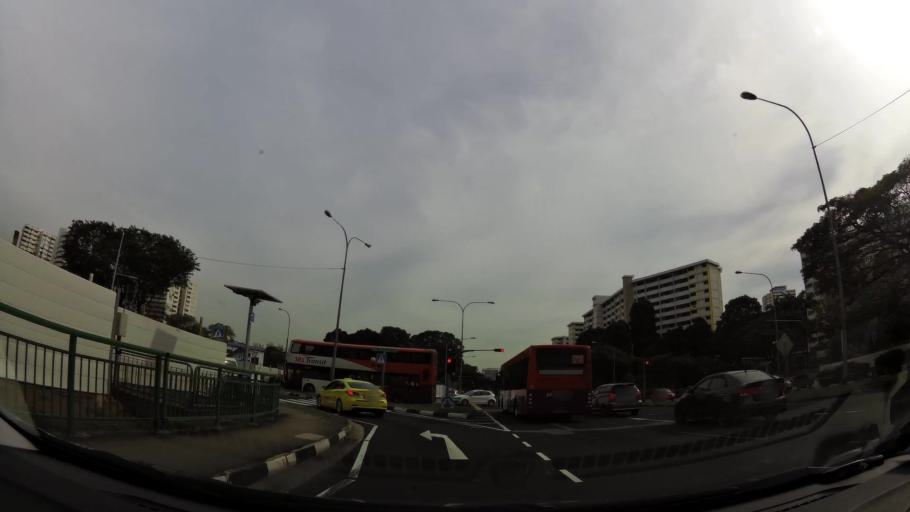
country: SG
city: Singapore
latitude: 1.3195
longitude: 103.7712
